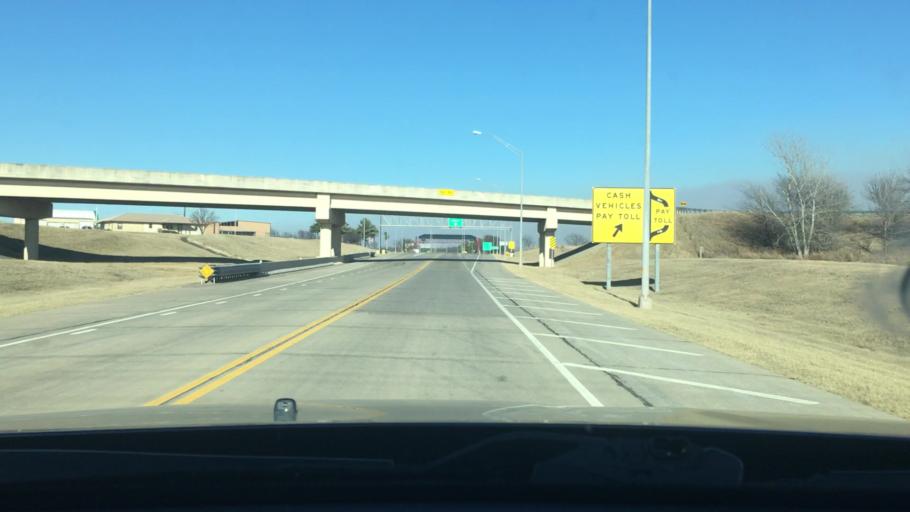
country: US
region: Oklahoma
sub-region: Murray County
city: Sulphur
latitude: 34.5635
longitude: -96.9328
